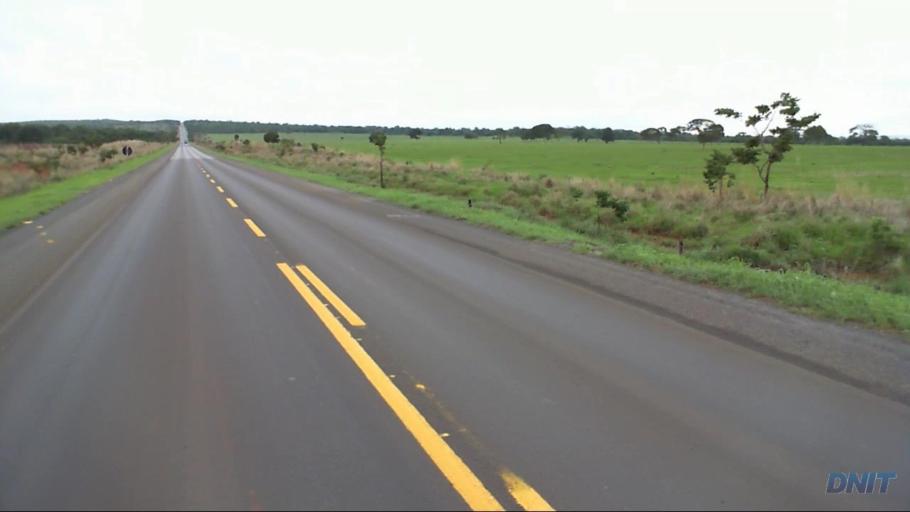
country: BR
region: Goias
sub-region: Padre Bernardo
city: Padre Bernardo
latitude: -15.1736
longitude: -48.3943
